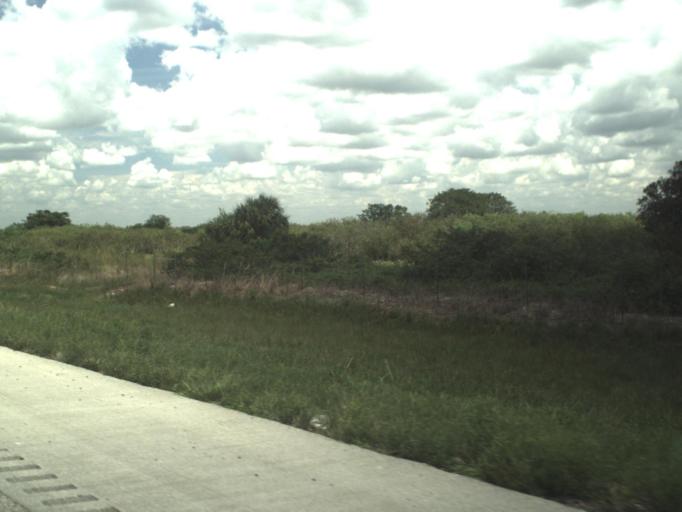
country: US
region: Florida
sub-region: Broward County
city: Weston
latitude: 26.1465
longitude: -80.5905
